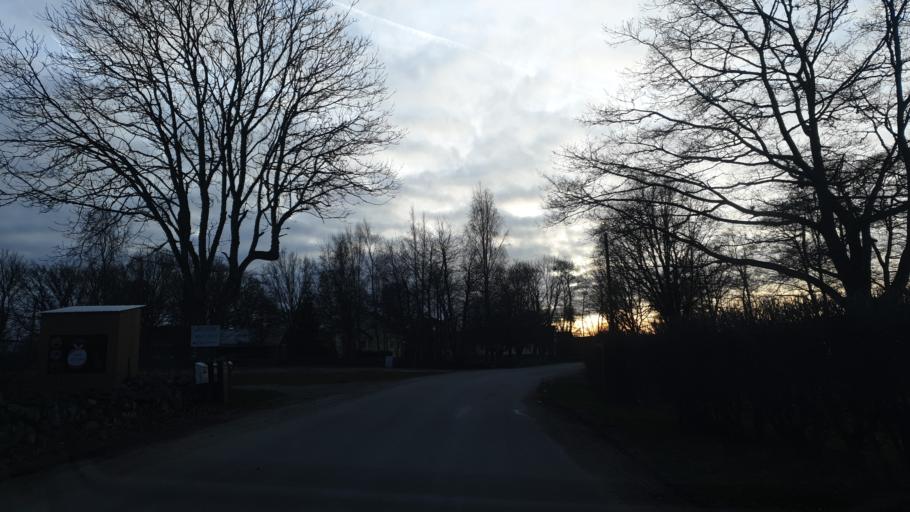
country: SE
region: Blekinge
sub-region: Karlskrona Kommun
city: Jaemjoe
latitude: 56.1523
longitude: 15.9047
